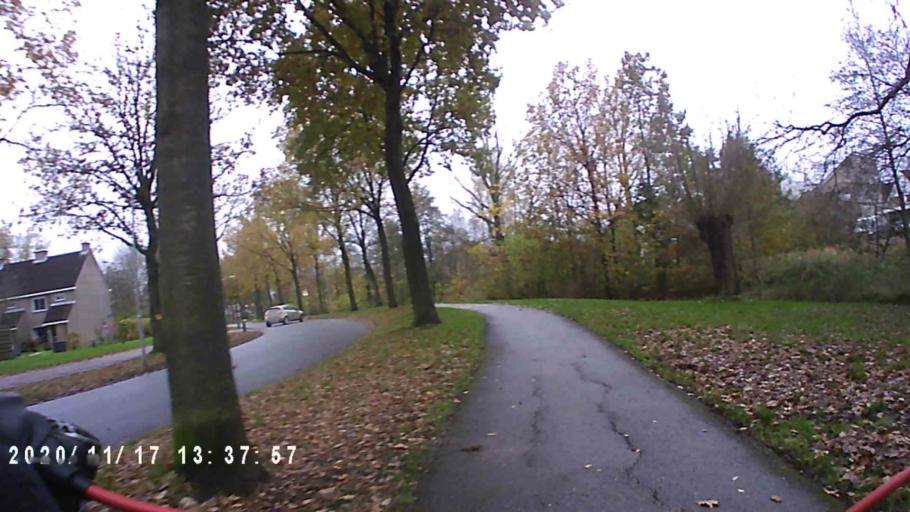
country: NL
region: Groningen
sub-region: Gemeente Zuidhorn
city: Zuidhorn
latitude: 53.2455
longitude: 6.3931
